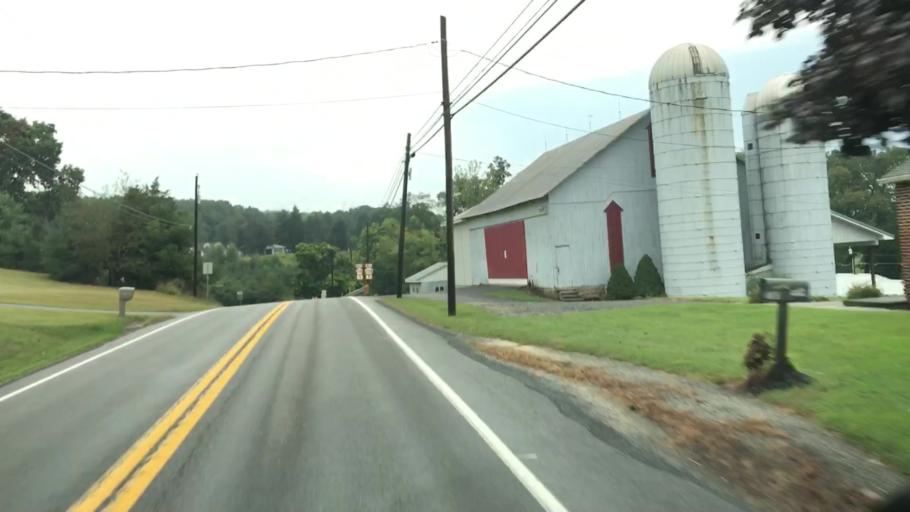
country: US
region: Pennsylvania
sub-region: Perry County
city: New Bloomfield
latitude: 40.3848
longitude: -77.1438
